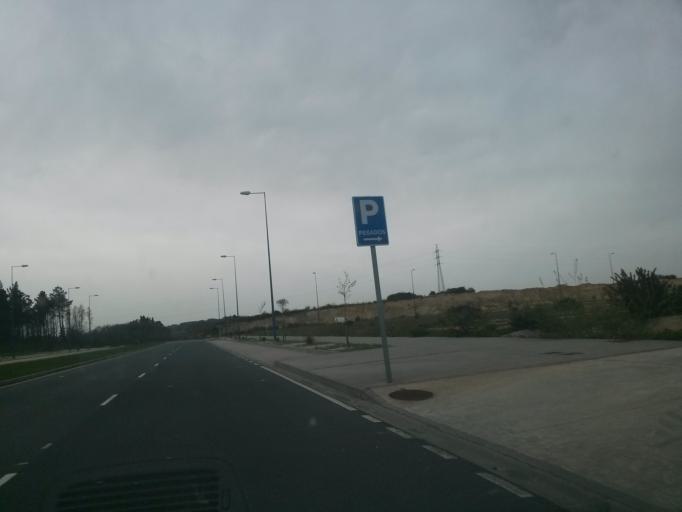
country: ES
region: Galicia
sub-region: Provincia de Lugo
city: Lugo
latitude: 43.0458
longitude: -7.5523
